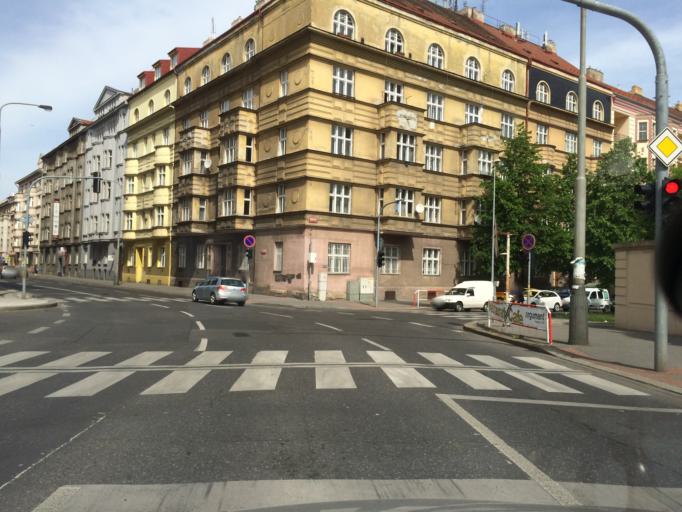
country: CZ
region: Praha
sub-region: Praha 1
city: Mala Strana
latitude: 50.0999
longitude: 14.4045
